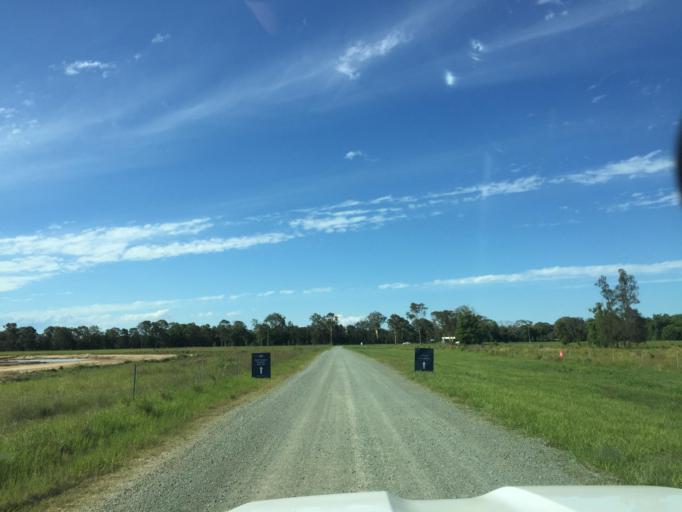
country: AU
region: Queensland
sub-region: Moreton Bay
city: Morayfield
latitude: -27.1103
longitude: 152.9930
